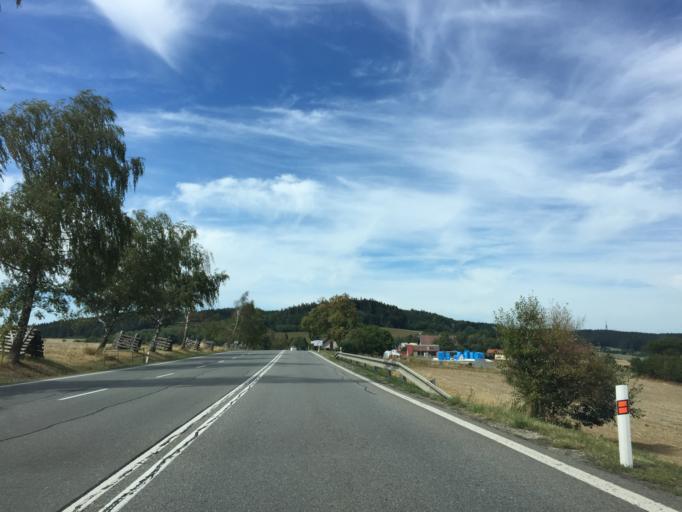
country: CZ
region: Central Bohemia
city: Votice
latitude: 49.5656
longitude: 14.6612
